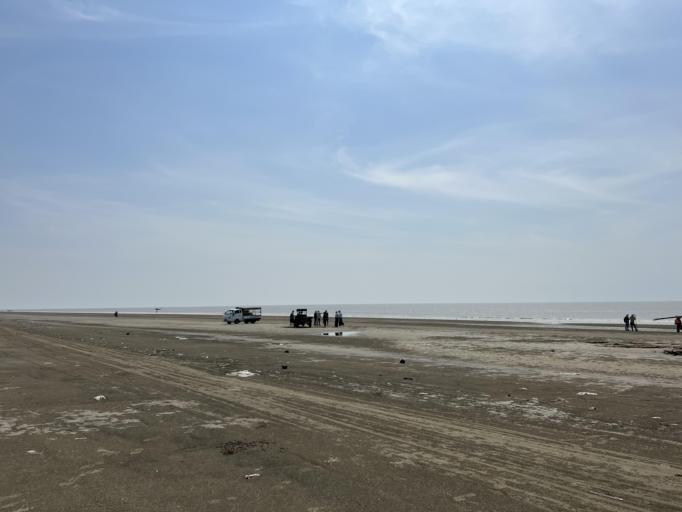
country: MM
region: Ayeyarwady
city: Pyapon
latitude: 15.8986
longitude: 95.6152
